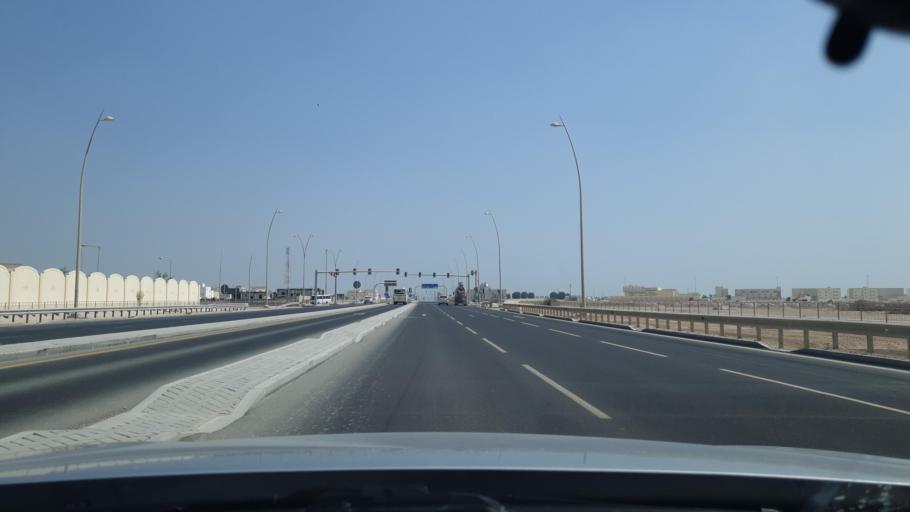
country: QA
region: Al Khawr
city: Al Khawr
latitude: 25.6616
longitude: 51.4909
